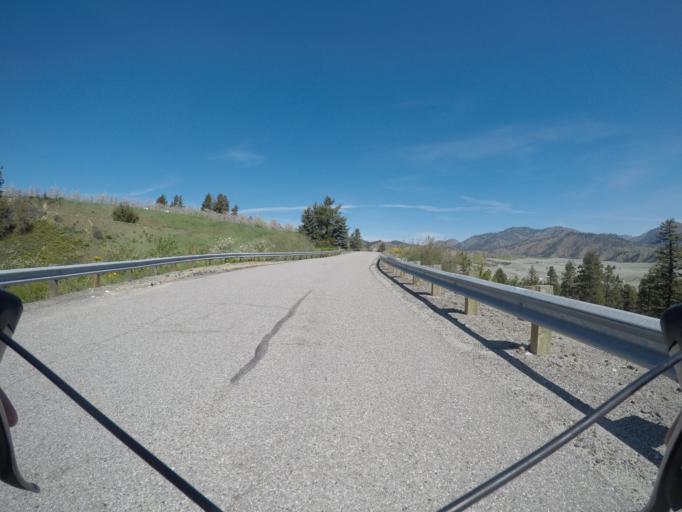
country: US
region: Washington
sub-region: Chelan County
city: Leavenworth
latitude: 47.5452
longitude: -120.5793
